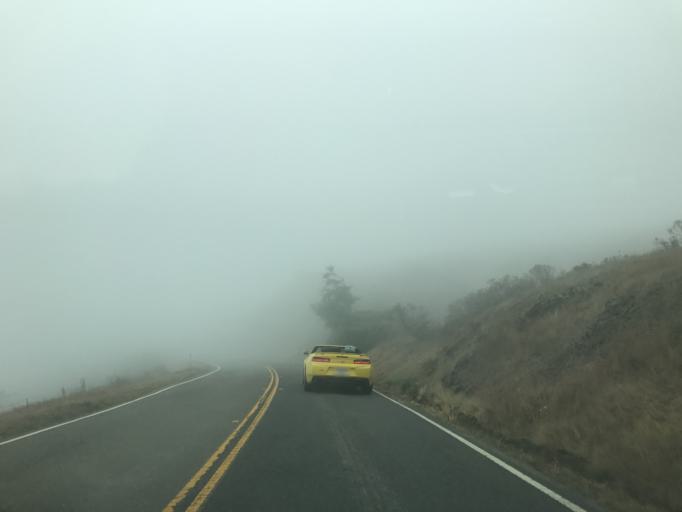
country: US
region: California
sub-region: Sonoma County
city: Monte Rio
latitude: 38.4756
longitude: -123.1583
